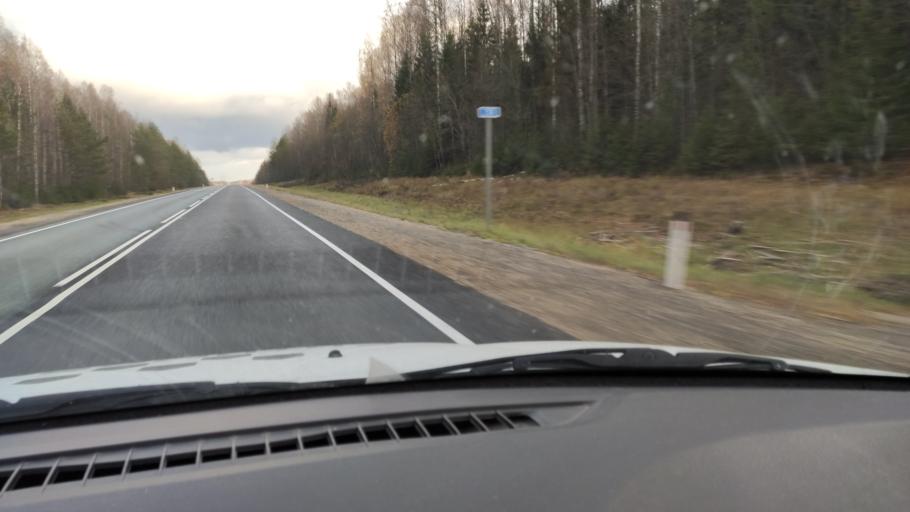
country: RU
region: Kirov
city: Chernaya Kholunitsa
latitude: 58.7989
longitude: 51.8663
